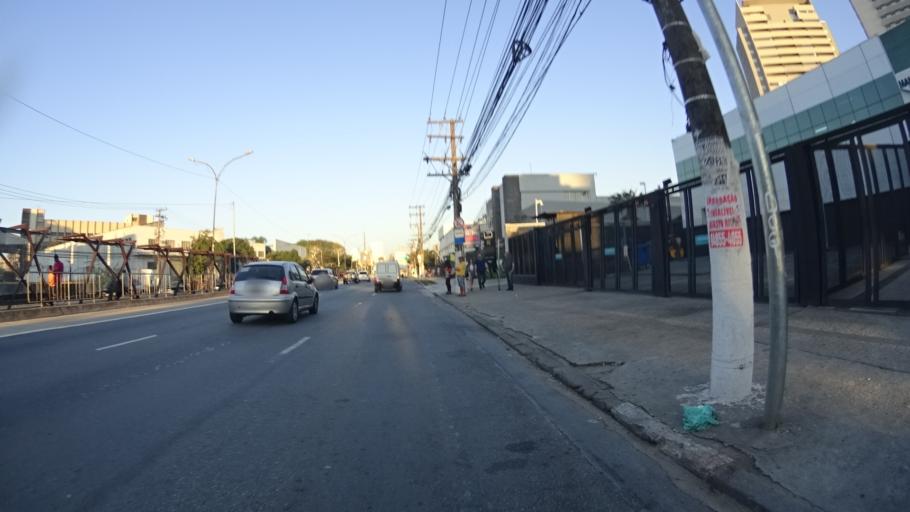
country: BR
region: Sao Paulo
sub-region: Sao Paulo
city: Sao Paulo
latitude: -23.5189
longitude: -46.6767
